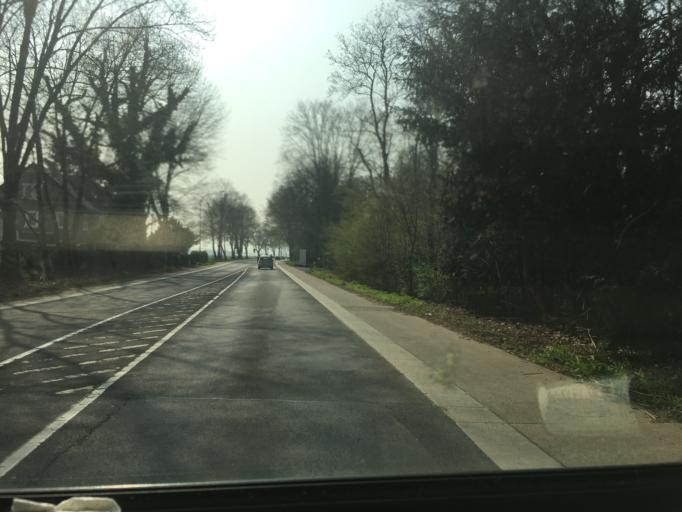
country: DE
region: North Rhine-Westphalia
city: Wesseling
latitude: 50.8025
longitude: 6.9903
